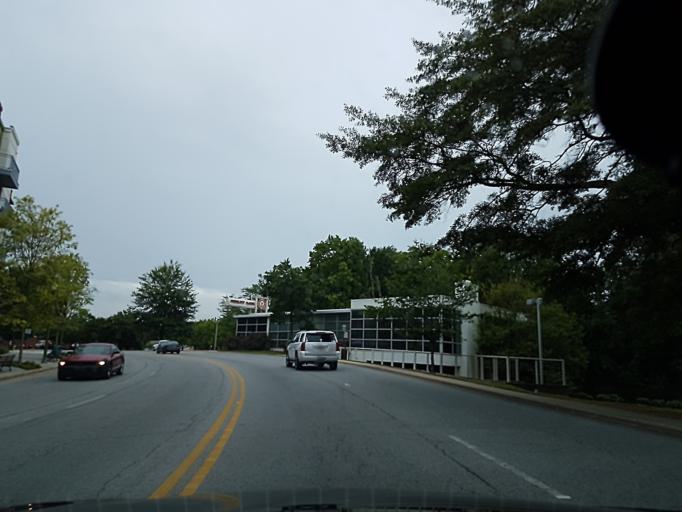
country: US
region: Georgia
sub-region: DeKalb County
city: Decatur
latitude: 33.7776
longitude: -84.2985
